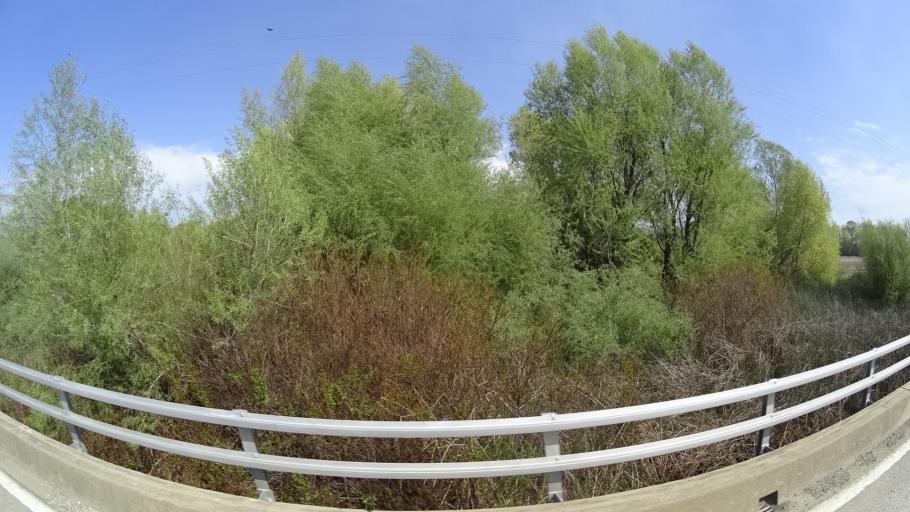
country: US
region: California
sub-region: Butte County
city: Biggs
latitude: 39.4641
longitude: -121.9245
